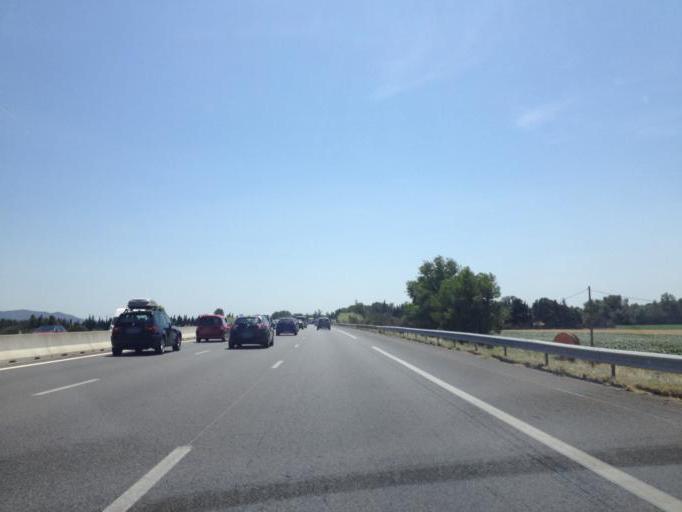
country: FR
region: Rhone-Alpes
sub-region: Departement de la Drome
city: La Garde-Adhemar
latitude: 44.4111
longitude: 4.7300
